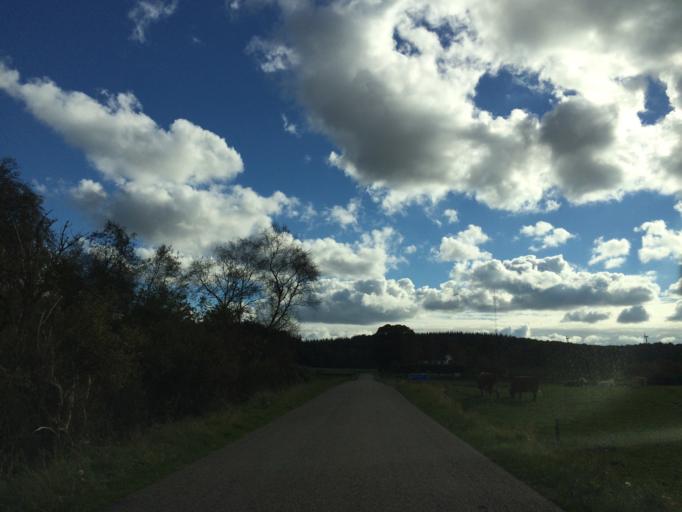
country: DK
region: Central Jutland
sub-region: Skanderborg Kommune
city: Ry
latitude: 56.1583
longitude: 9.7539
